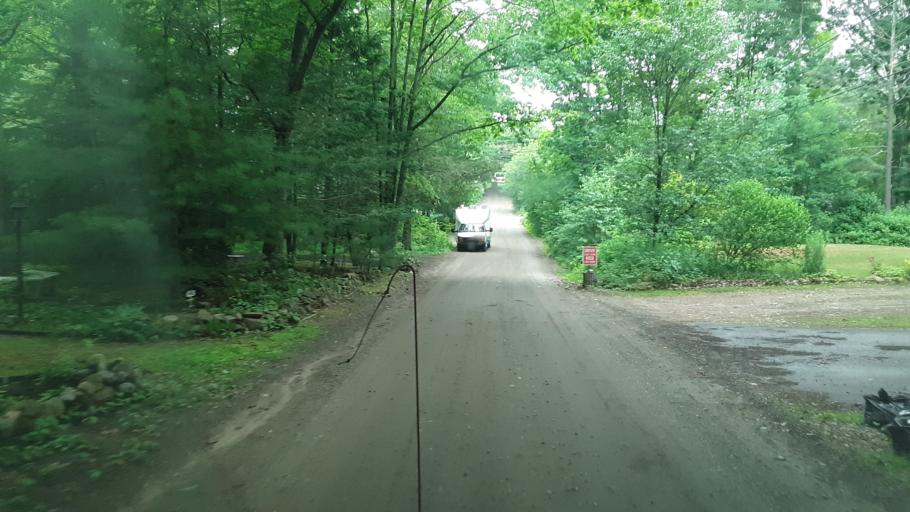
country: US
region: Maine
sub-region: York County
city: Cape Neddick
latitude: 43.1760
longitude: -70.6292
